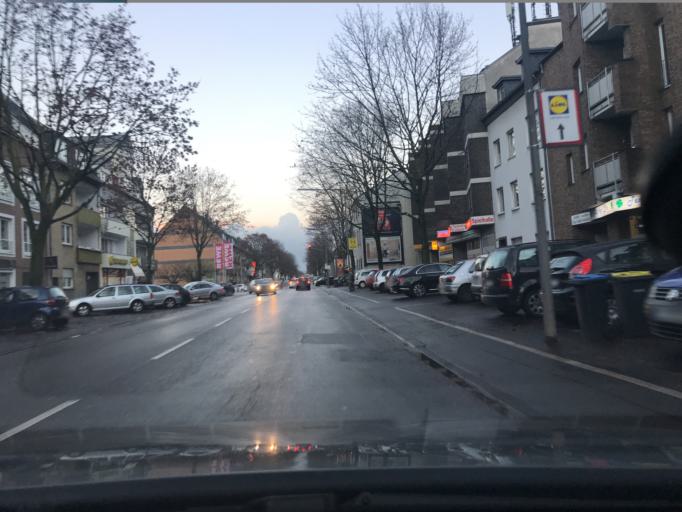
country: DE
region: North Rhine-Westphalia
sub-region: Regierungsbezirk Koln
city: Merheim
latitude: 50.9718
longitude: 7.0514
